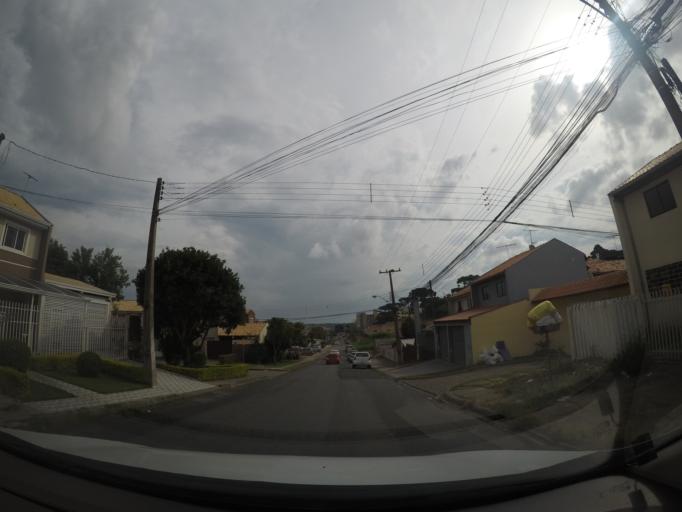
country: BR
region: Parana
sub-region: Sao Jose Dos Pinhais
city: Sao Jose dos Pinhais
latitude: -25.5201
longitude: -49.2583
